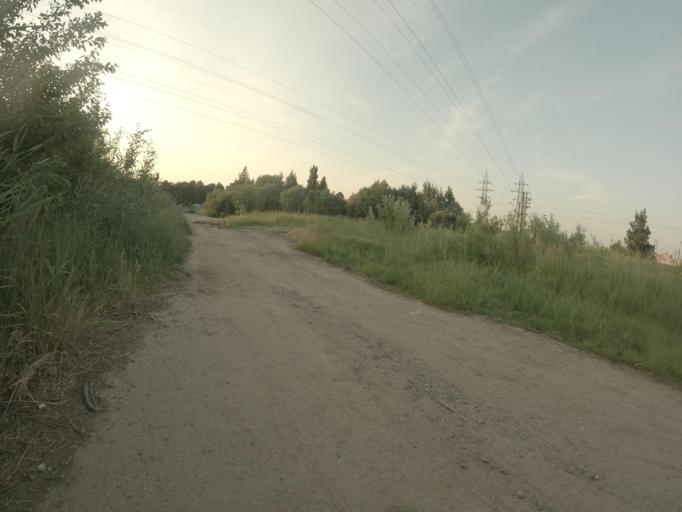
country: RU
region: St.-Petersburg
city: Krasnogvargeisky
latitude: 59.9396
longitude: 30.4469
